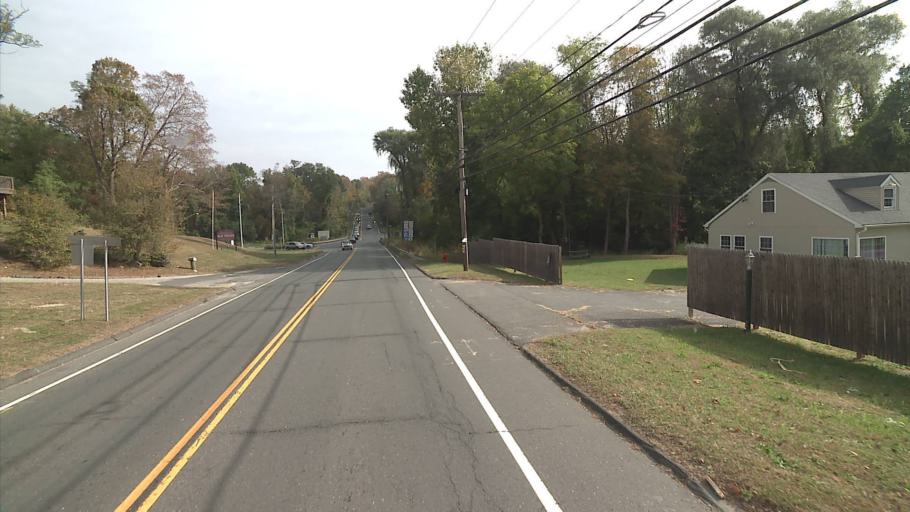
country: US
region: Connecticut
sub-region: Fairfield County
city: Newtown
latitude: 41.4180
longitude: -73.3554
